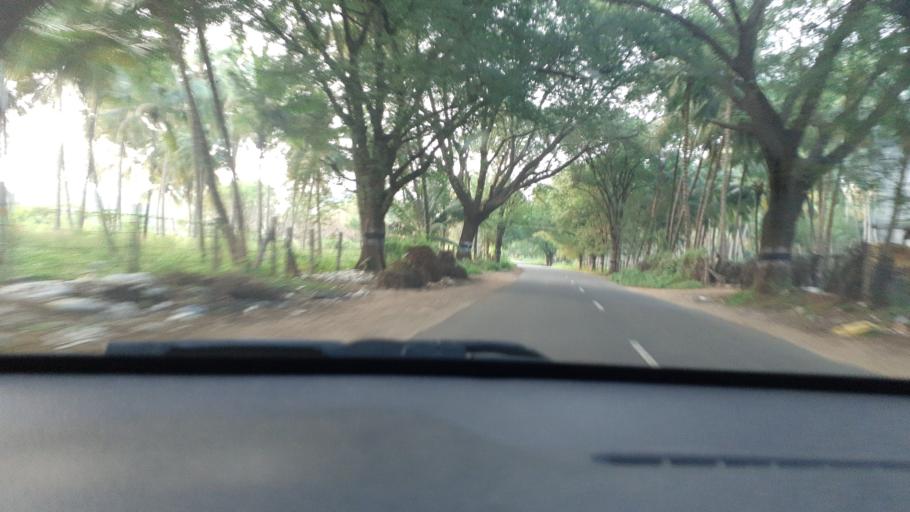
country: IN
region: Tamil Nadu
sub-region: Dindigul
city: Palani
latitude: 10.4257
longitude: 77.5327
